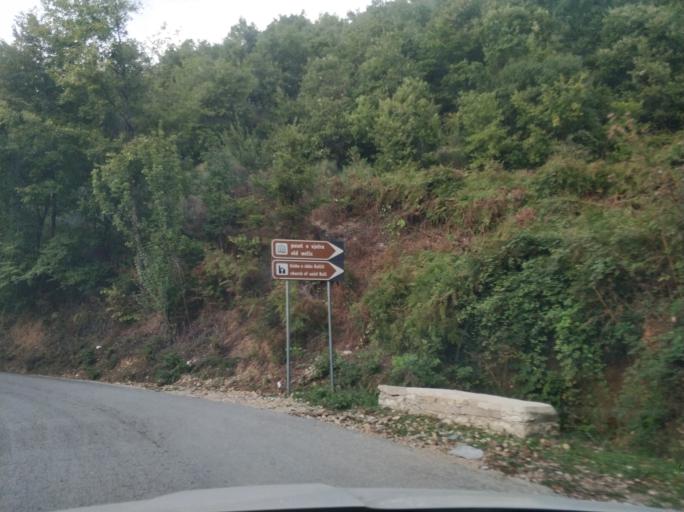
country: AL
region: Vlore
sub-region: Rrethi i Sarandes
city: Dhiver
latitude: 39.9185
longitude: 20.2015
